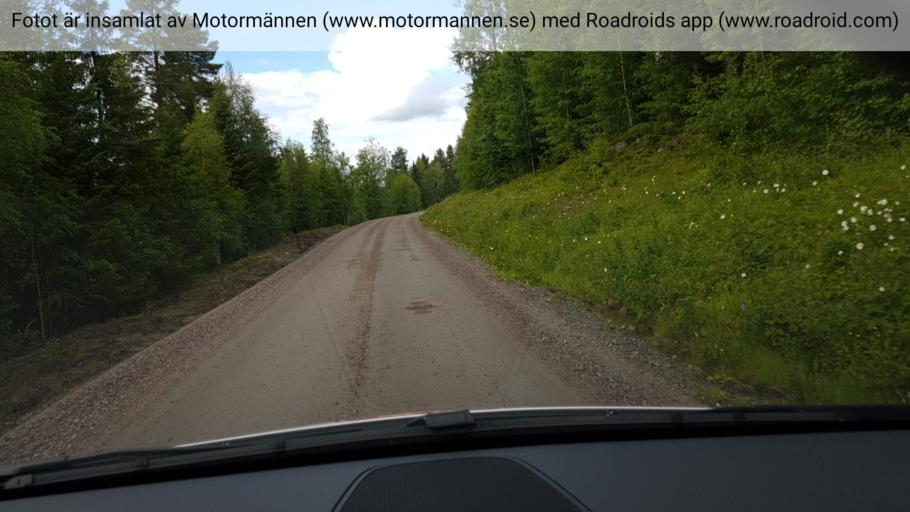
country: SE
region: Jaemtland
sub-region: Stroemsunds Kommun
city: Stroemsund
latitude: 64.0017
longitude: 15.9683
